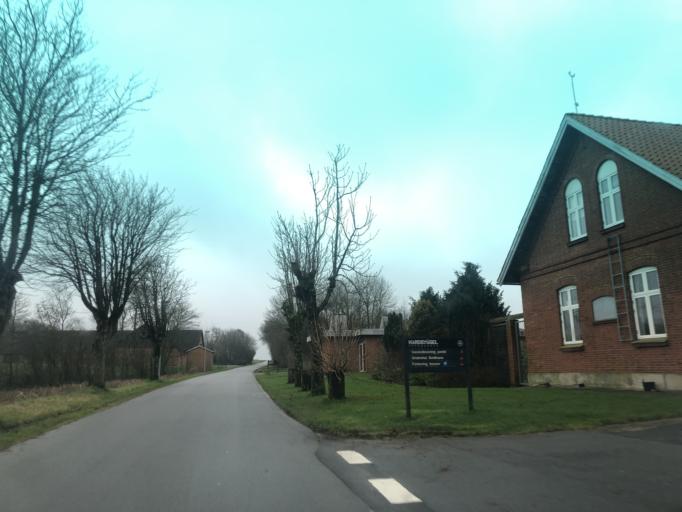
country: DK
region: Central Jutland
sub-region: Struer Kommune
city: Struer
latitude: 56.4480
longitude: 8.5889
